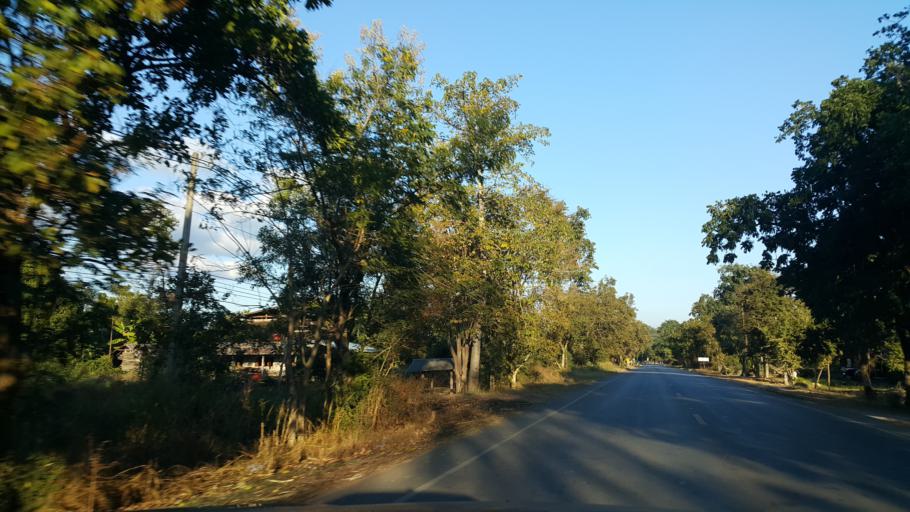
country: TH
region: Sukhothai
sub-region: Amphoe Si Satchanalai
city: Si Satchanalai
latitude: 17.5521
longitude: 99.8689
